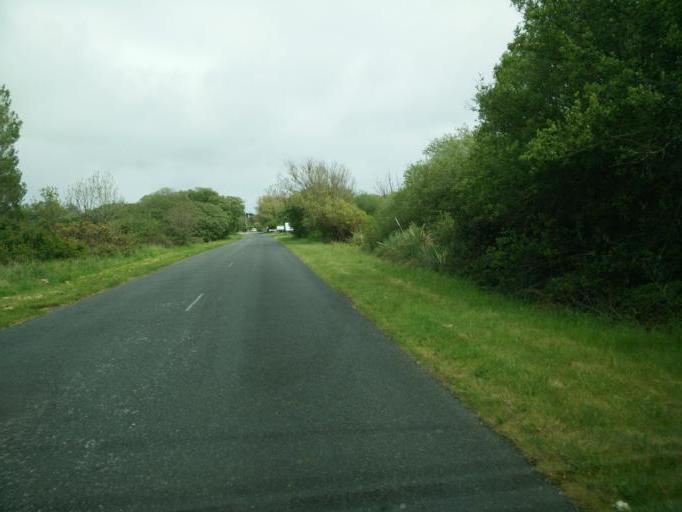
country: FR
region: Brittany
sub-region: Departement du Finistere
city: Plobannalec-Lesconil
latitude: 47.8034
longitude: -4.1982
